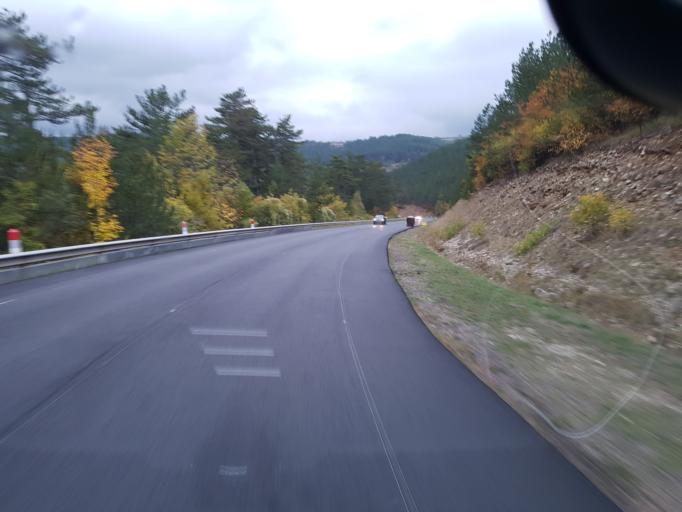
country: FR
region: Languedoc-Roussillon
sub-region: Departement de la Lozere
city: Mende
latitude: 44.5353
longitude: 3.5790
